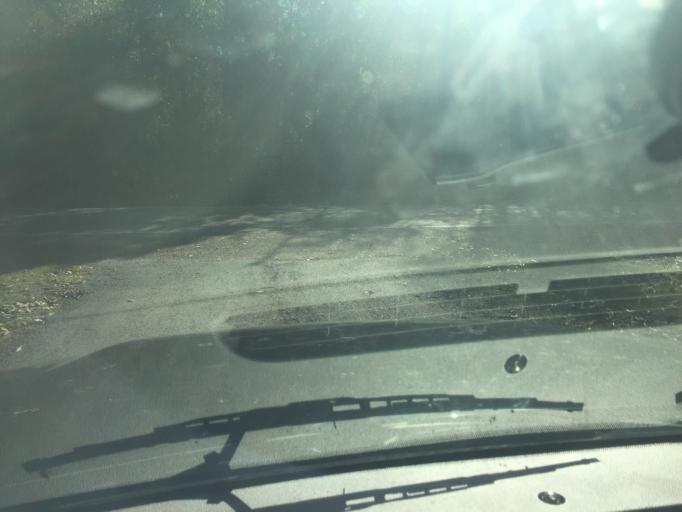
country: US
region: Louisiana
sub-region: Saint Tammany Parish
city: Slidell
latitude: 30.3134
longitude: -89.7458
